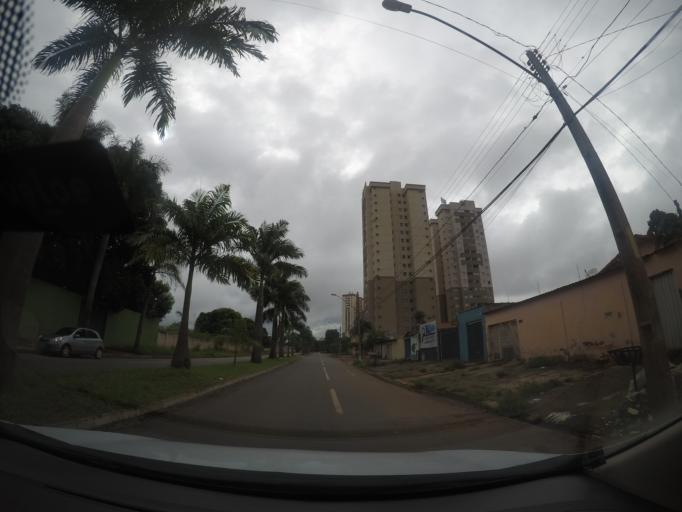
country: BR
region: Goias
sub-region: Goiania
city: Goiania
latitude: -16.7298
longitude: -49.2863
